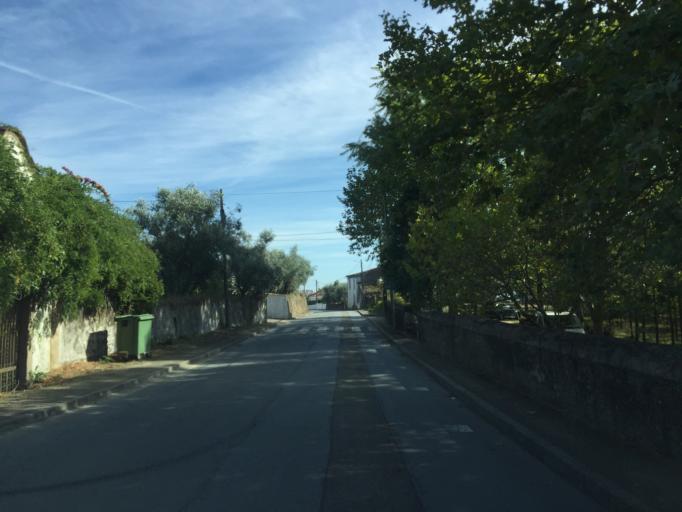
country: PT
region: Portalegre
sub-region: Portalegre
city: Portalegre
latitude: 39.3087
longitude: -7.4390
